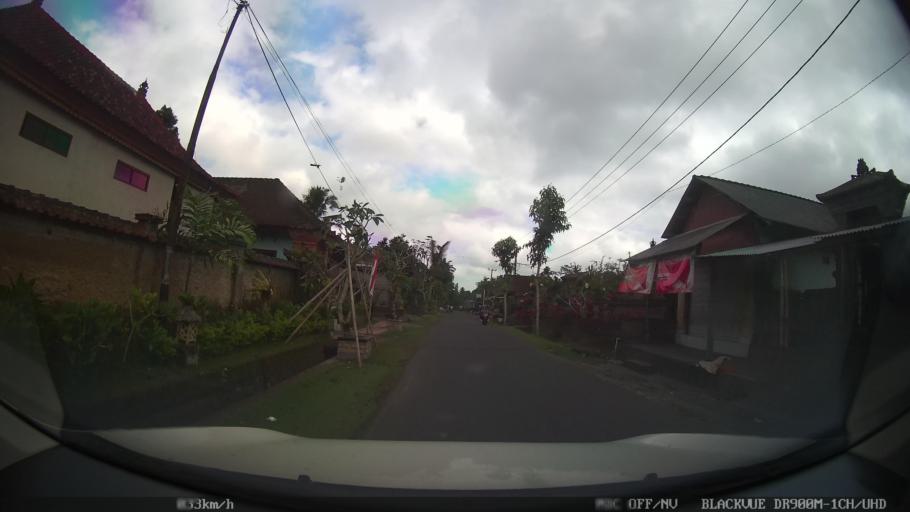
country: ID
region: Bali
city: Banjar Petak
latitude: -8.4376
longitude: 115.3215
